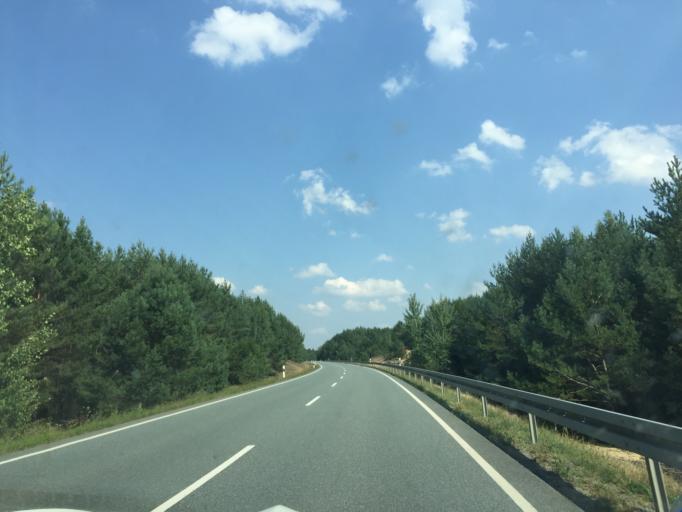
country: DE
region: Saxony
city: Uhyst
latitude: 51.3939
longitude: 14.5048
